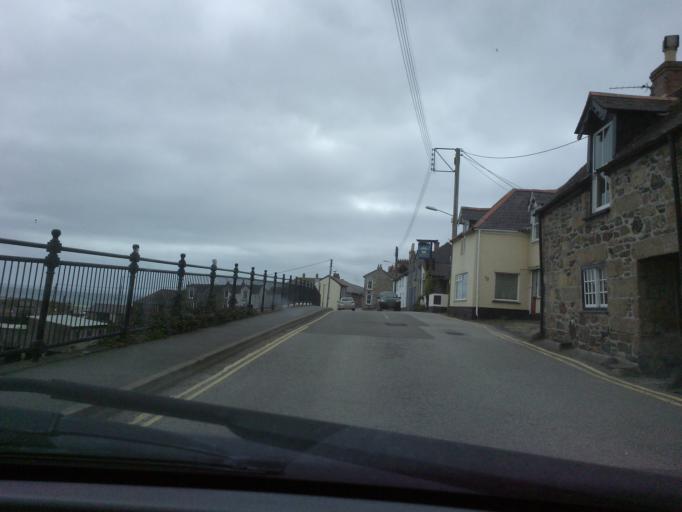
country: GB
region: England
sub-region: Cornwall
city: Penzance
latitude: 50.1018
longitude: -5.5467
